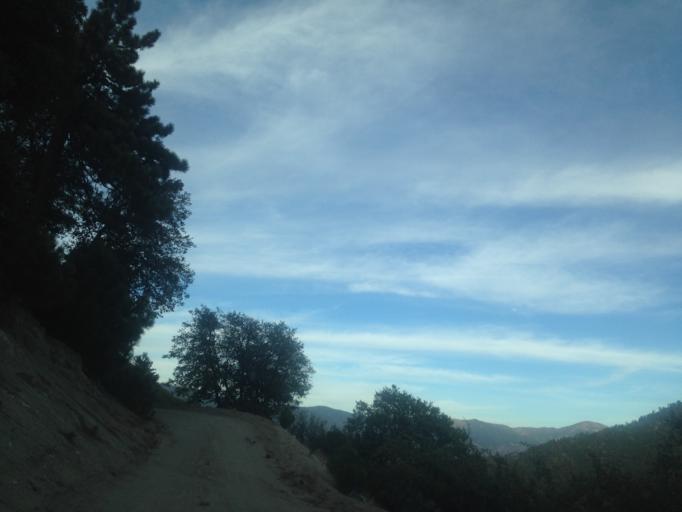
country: US
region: California
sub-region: San Bernardino County
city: Yucaipa
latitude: 34.1404
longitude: -116.9934
